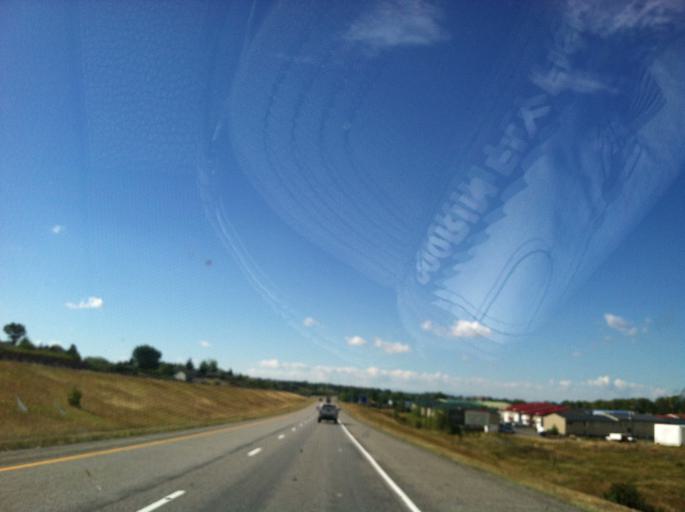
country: US
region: Montana
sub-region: Gallatin County
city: Bozeman
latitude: 45.6696
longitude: -110.9931
